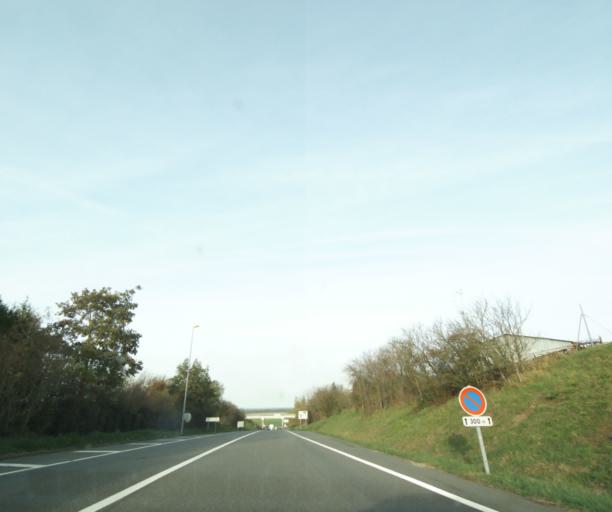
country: FR
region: Lorraine
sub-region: Departement de la Meuse
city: Etain
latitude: 49.1298
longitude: 5.6220
